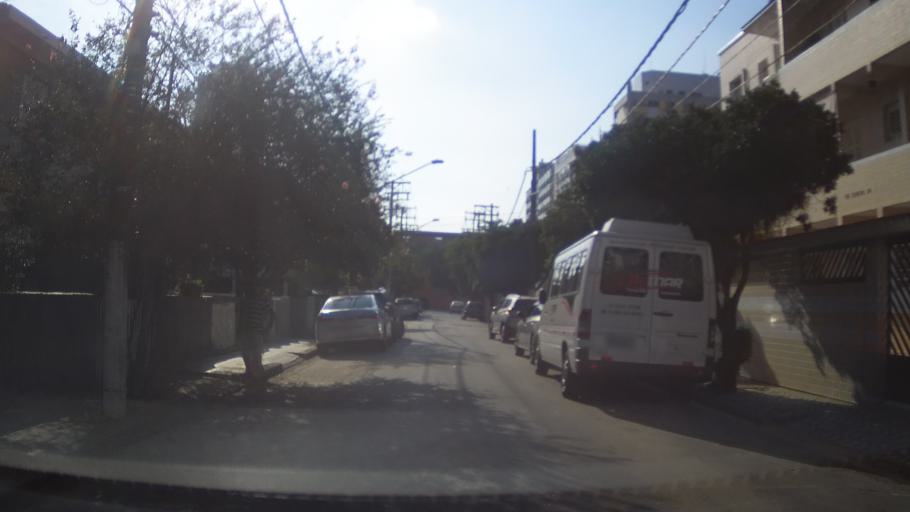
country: BR
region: Sao Paulo
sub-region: Santos
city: Santos
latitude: -23.9640
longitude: -46.3266
